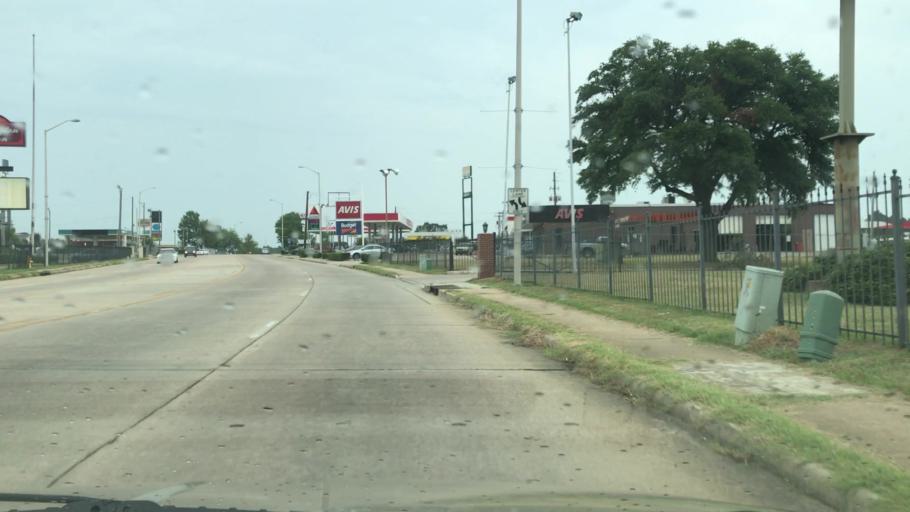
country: US
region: Louisiana
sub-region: Caddo Parish
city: Shreveport
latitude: 32.4576
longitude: -93.8268
